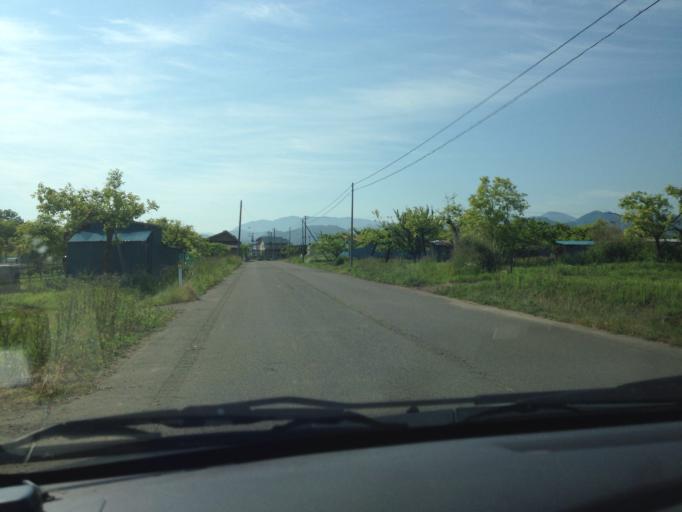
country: JP
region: Fukushima
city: Kitakata
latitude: 37.4536
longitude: 139.8198
